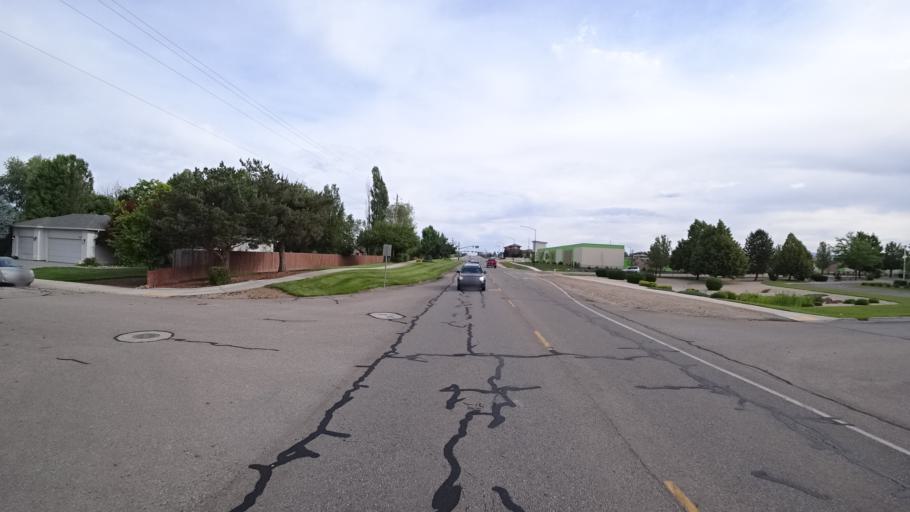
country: US
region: Idaho
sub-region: Ada County
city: Meridian
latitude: 43.5870
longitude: -116.3746
